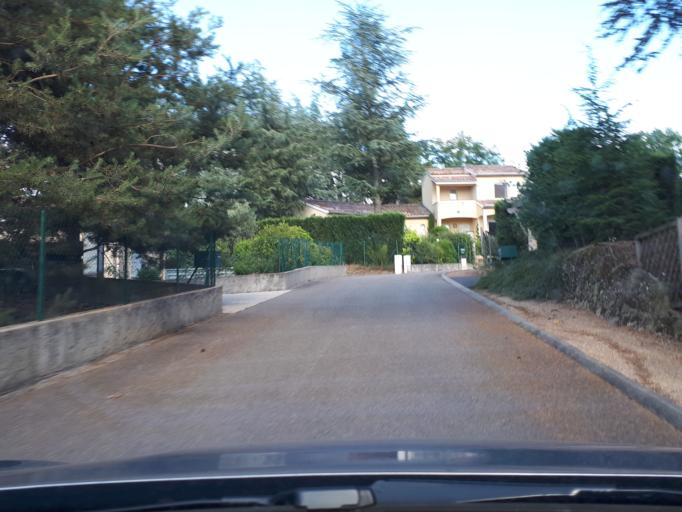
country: FR
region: Rhone-Alpes
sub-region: Departement de la Loire
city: Civens
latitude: 45.7598
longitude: 4.2779
